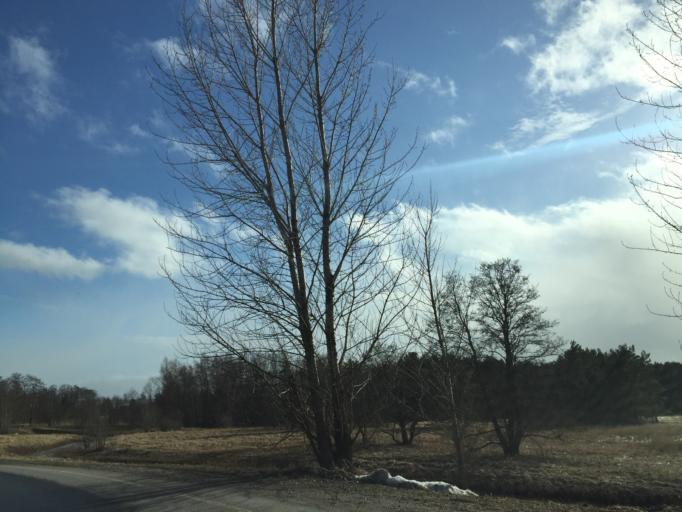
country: EE
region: Laeaene
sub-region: Haapsalu linn
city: Haapsalu
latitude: 58.9392
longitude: 23.5304
